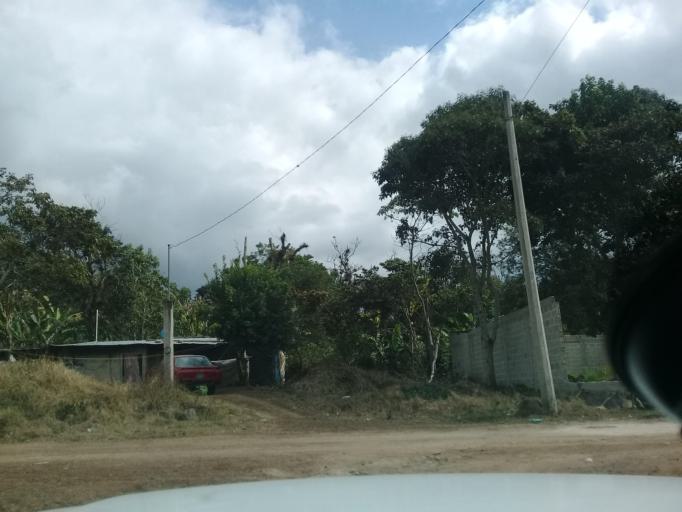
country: MX
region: Veracruz
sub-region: Xalapa
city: Fraccionamiento las Fuentes
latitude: 19.4745
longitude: -96.8761
